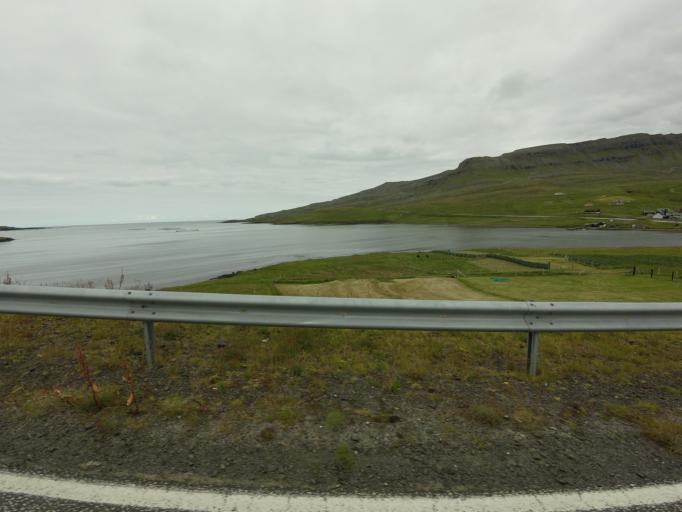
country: FO
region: Suduroy
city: Tvoroyri
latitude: 61.5368
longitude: -6.8108
